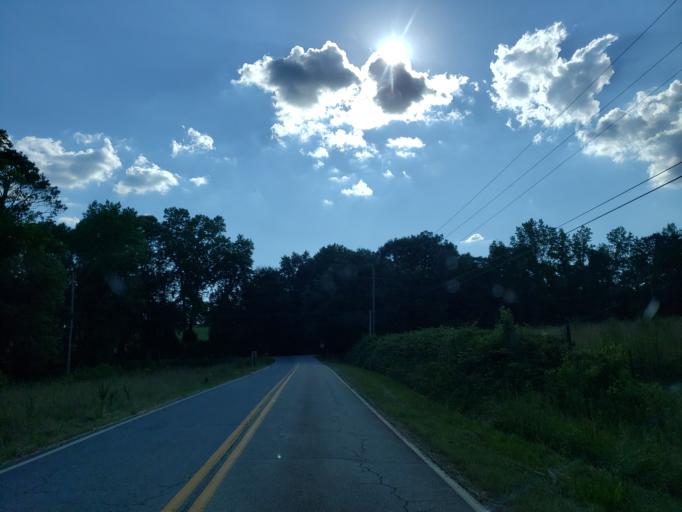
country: US
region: Georgia
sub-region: Carroll County
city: Carrollton
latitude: 33.6500
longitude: -85.1097
